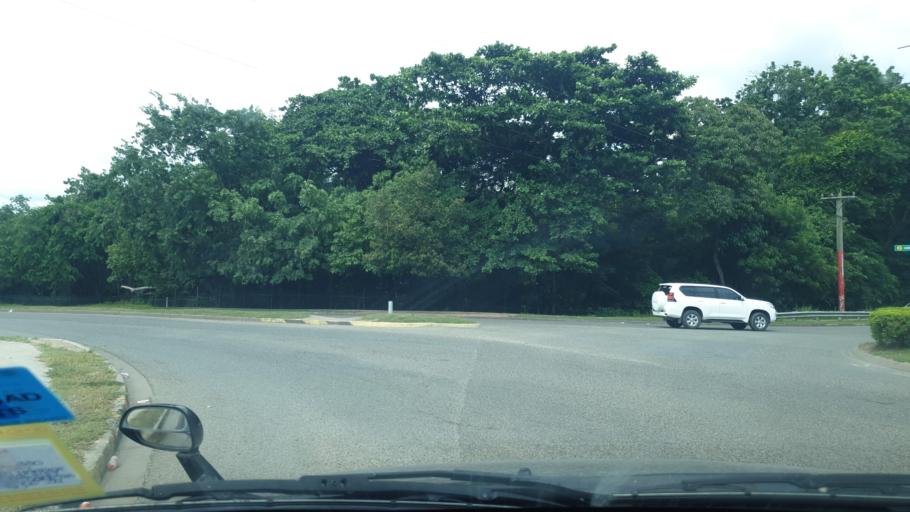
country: PG
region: National Capital
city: Port Moresby
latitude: -9.4087
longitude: 147.1644
